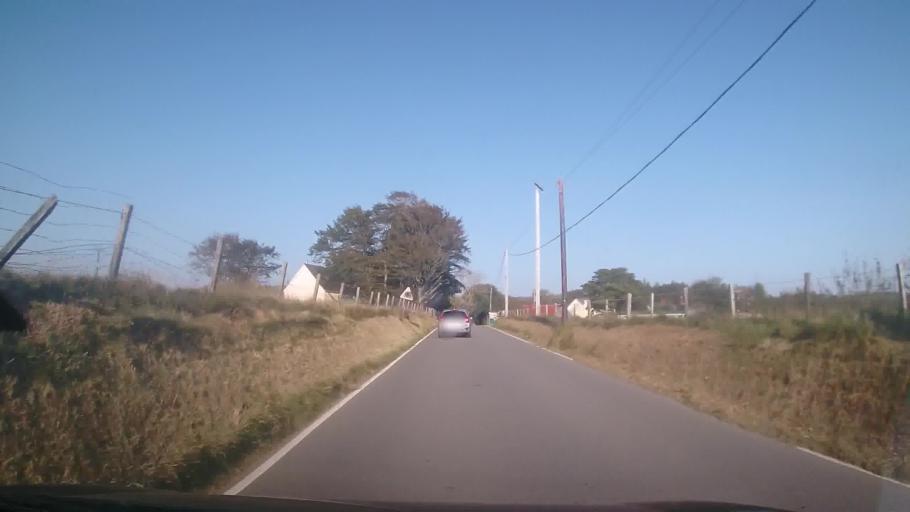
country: GB
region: Wales
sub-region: County of Ceredigion
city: Lledrod
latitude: 52.2954
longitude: -3.8525
